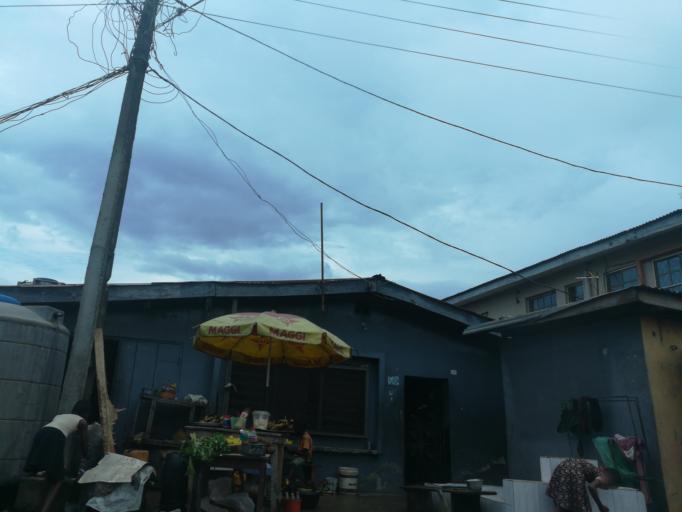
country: NG
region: Lagos
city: Agege
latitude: 6.6229
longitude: 3.3340
